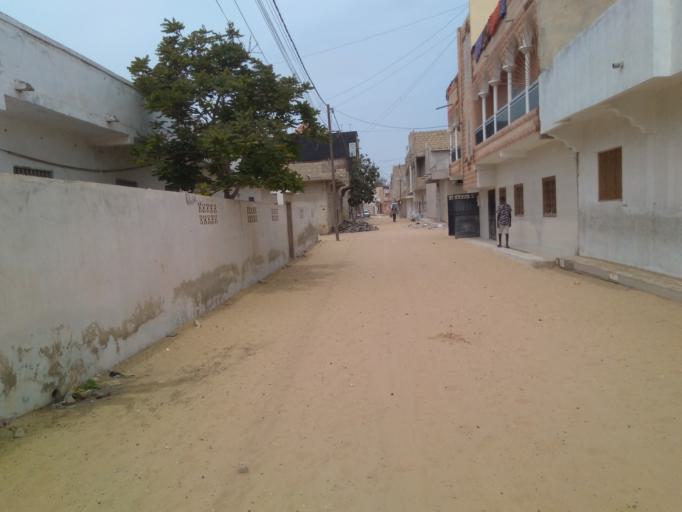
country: SN
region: Dakar
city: Pikine
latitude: 14.8004
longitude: -17.3383
